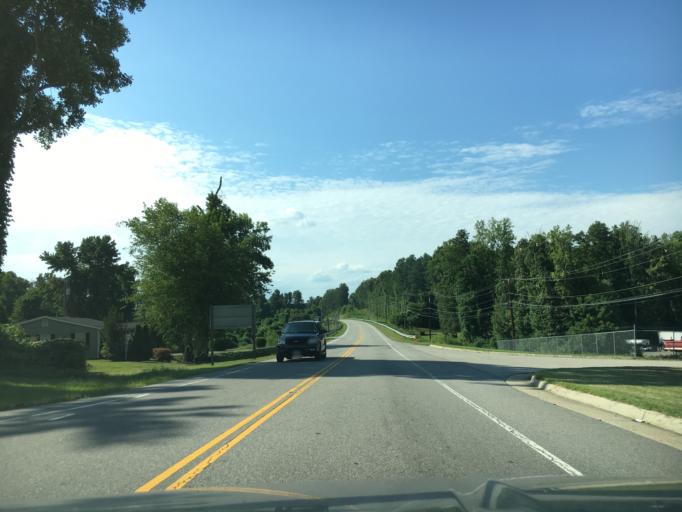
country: US
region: Virginia
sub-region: Halifax County
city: Halifax
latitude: 36.7749
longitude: -78.9205
